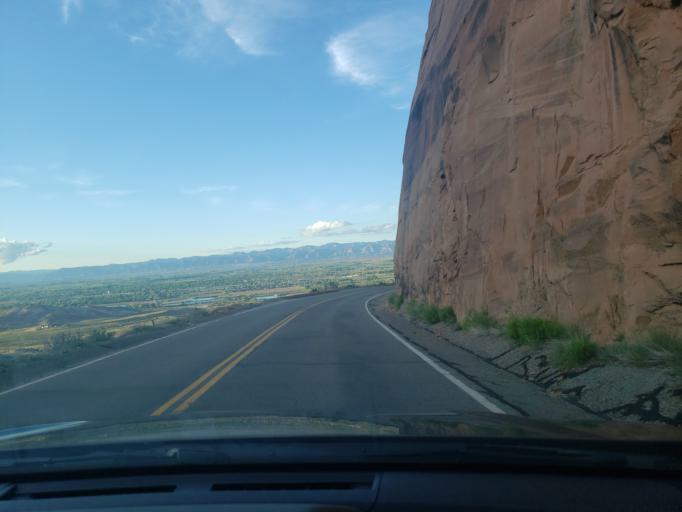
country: US
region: Colorado
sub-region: Mesa County
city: Fruita
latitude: 39.1145
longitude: -108.7304
